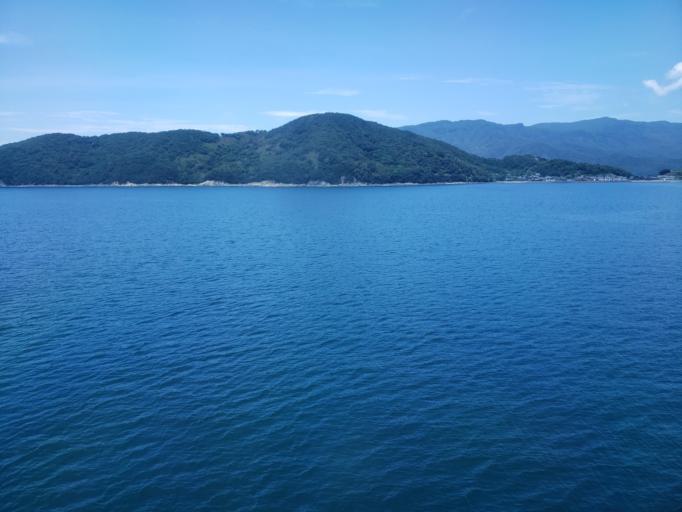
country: JP
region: Kagawa
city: Tonosho
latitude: 34.4443
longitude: 134.3068
